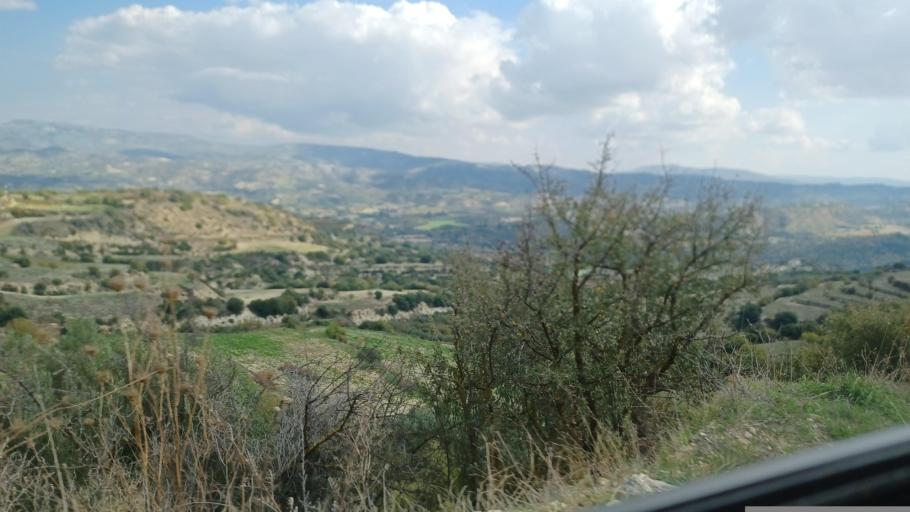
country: CY
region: Pafos
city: Mesogi
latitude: 34.8391
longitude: 32.5254
